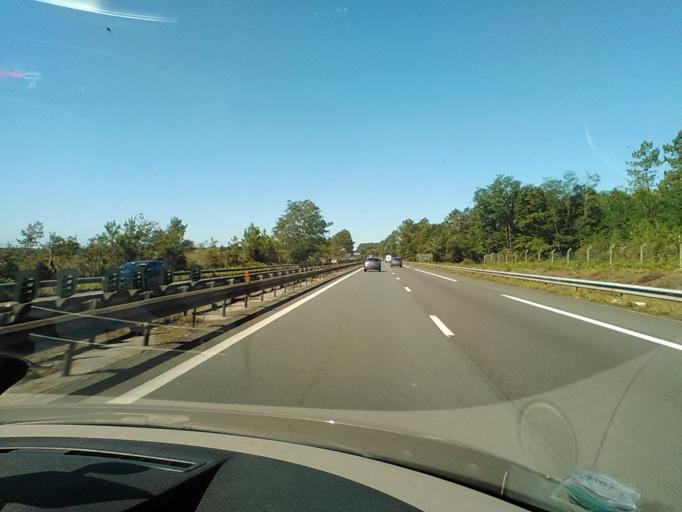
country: FR
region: Aquitaine
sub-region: Departement des Landes
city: Saint-Geours-de-Maremne
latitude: 43.6882
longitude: -1.2494
